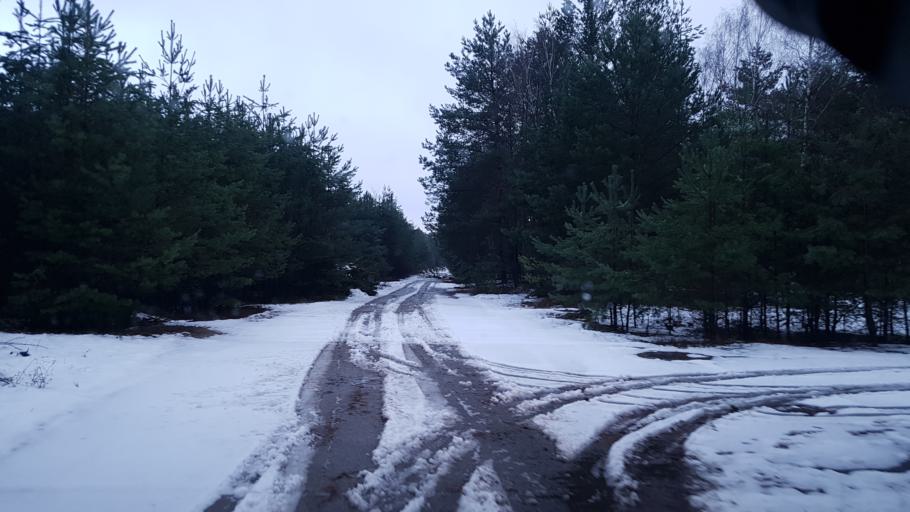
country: DE
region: Brandenburg
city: Janschwalde
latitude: 51.8842
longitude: 14.5470
